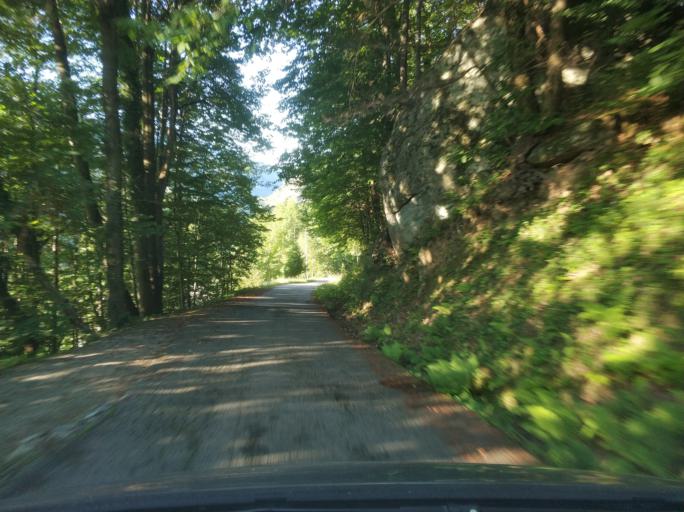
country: IT
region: Piedmont
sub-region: Provincia di Torino
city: Viu
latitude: 45.2212
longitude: 7.3923
